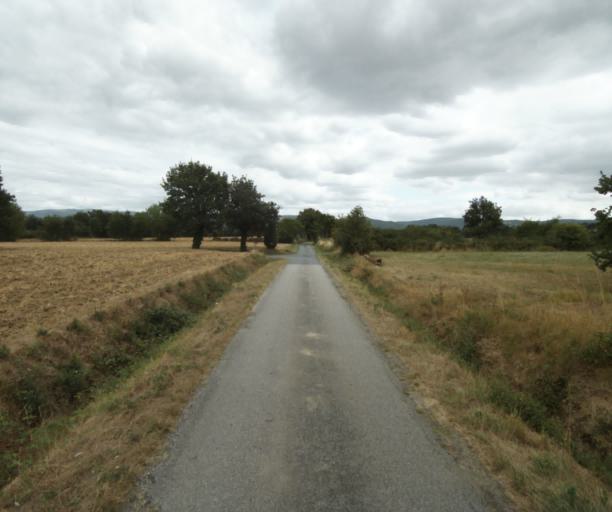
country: FR
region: Midi-Pyrenees
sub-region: Departement du Tarn
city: Soreze
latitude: 43.4829
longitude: 2.0438
